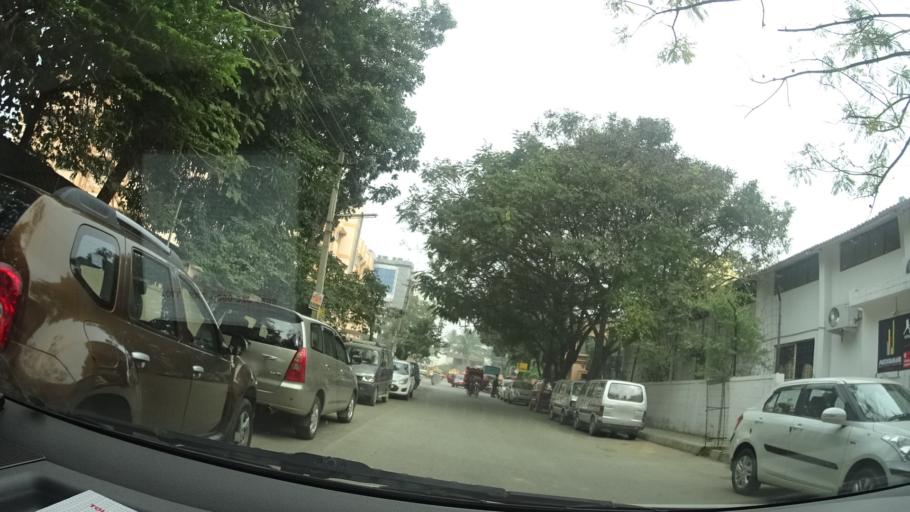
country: IN
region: Karnataka
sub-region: Bangalore Urban
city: Bangalore
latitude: 13.0248
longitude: 77.6287
